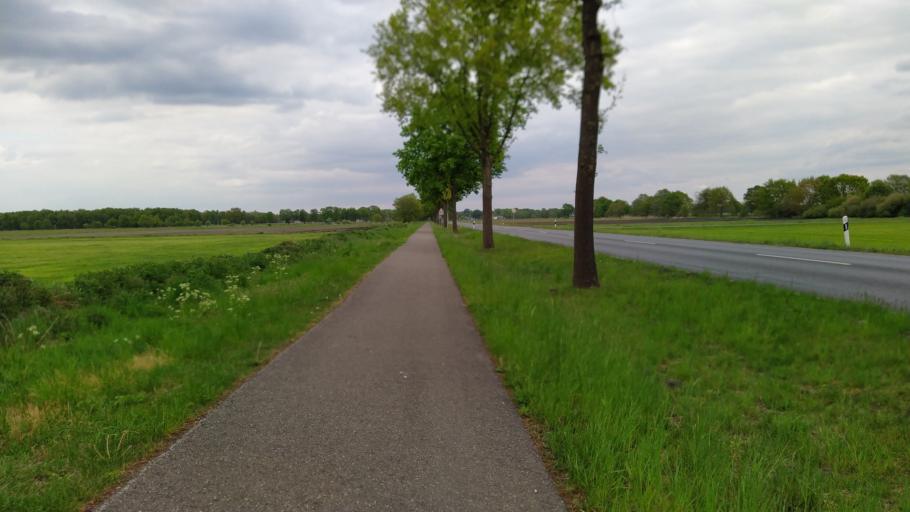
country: DE
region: Lower Saxony
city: Tarmstedt
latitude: 53.2109
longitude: 9.0444
